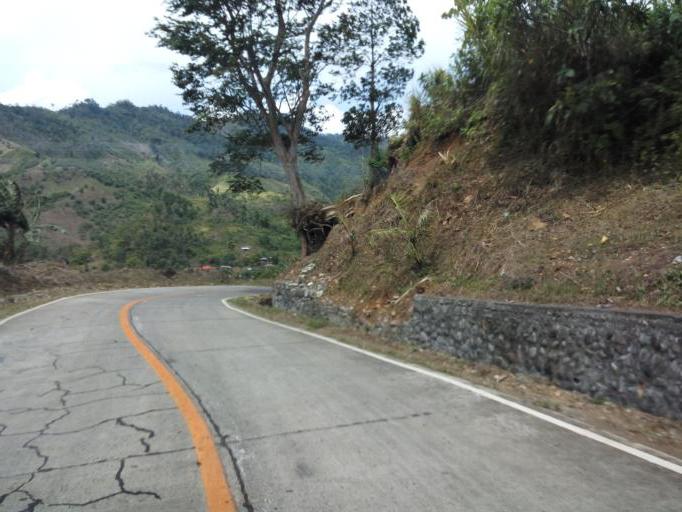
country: PH
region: Cagayan Valley
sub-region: Province of Quirino
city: Dumabato
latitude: 16.2543
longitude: 121.7153
